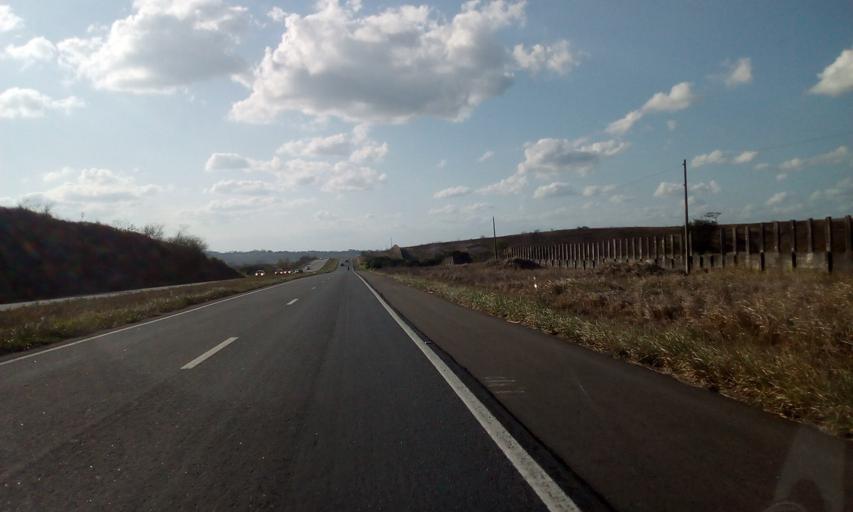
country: BR
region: Paraiba
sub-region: Cruz Do Espirito Santo
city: Cruz do Espirito Santo
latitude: -7.1948
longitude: -35.1743
